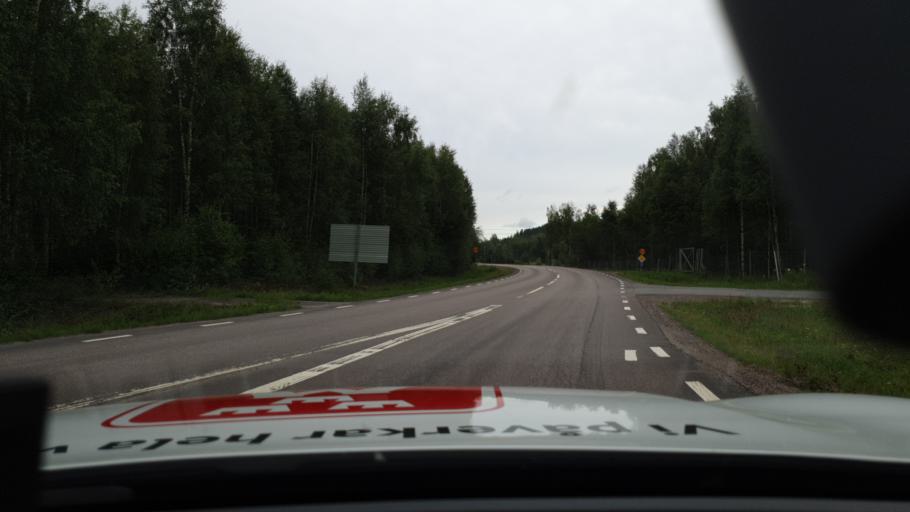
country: SE
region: Norrbotten
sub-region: Lulea Kommun
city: Sodra Sunderbyn
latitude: 65.5482
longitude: 21.8489
